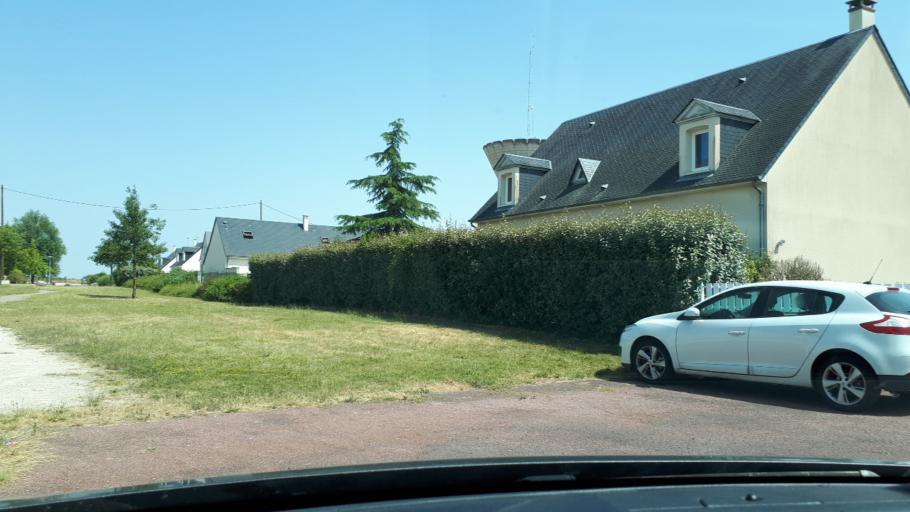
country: FR
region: Centre
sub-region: Departement du Loir-et-Cher
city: Vendome
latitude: 47.8142
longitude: 1.0498
